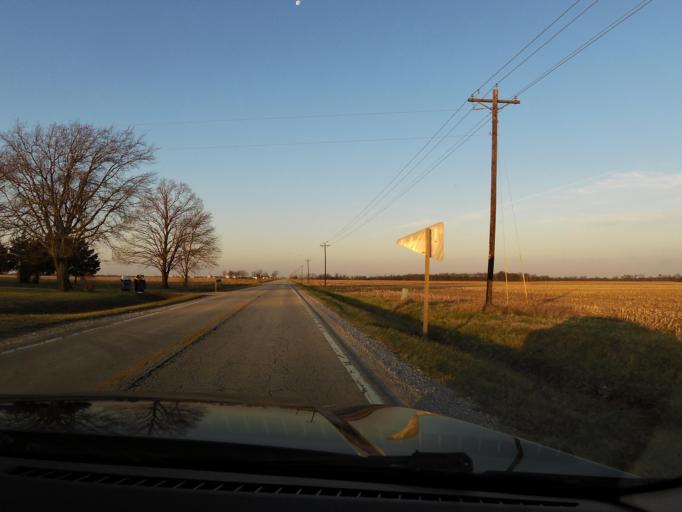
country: US
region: Illinois
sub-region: Marion County
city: Salem
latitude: 38.7653
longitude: -88.9880
